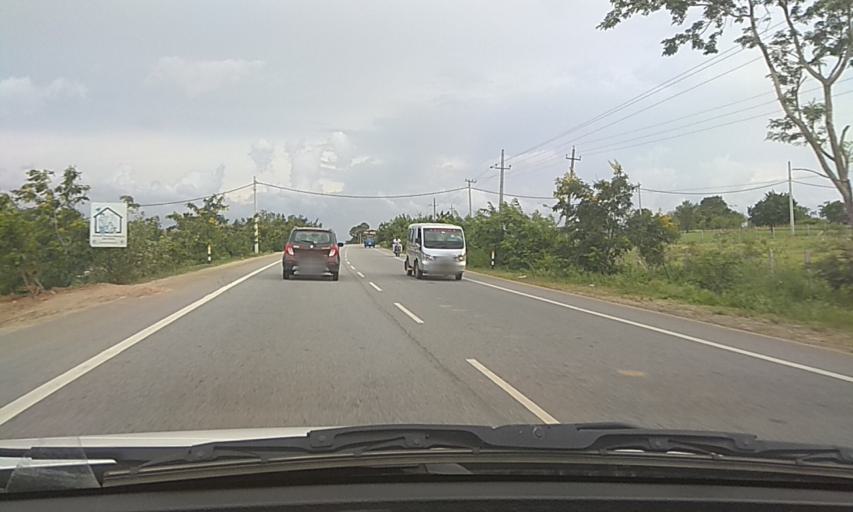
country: IN
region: Karnataka
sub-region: Chamrajnagar
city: Gundlupet
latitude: 11.9511
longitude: 76.6707
